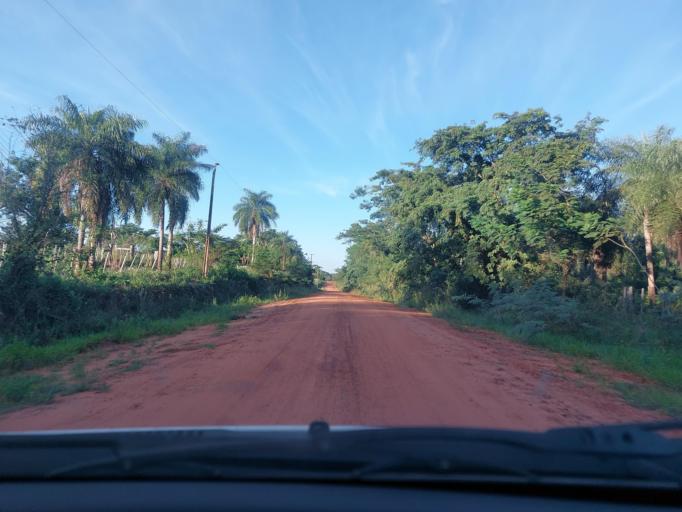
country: PY
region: San Pedro
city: Itacurubi del Rosario
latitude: -24.5445
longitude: -56.5847
